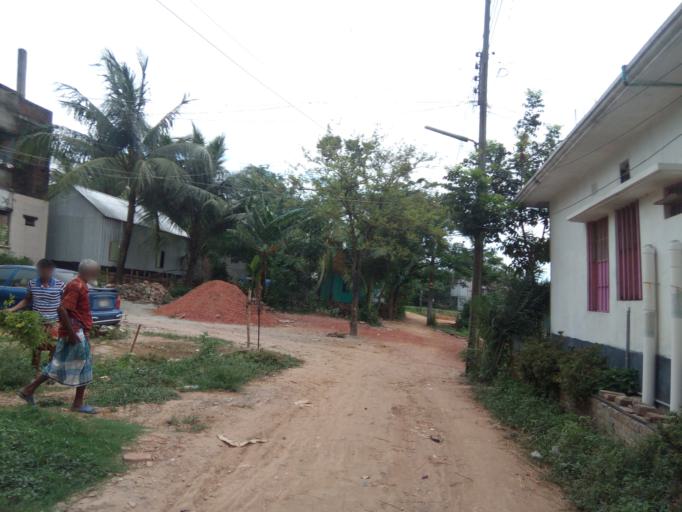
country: BD
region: Dhaka
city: Paltan
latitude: 23.7348
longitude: 90.4510
